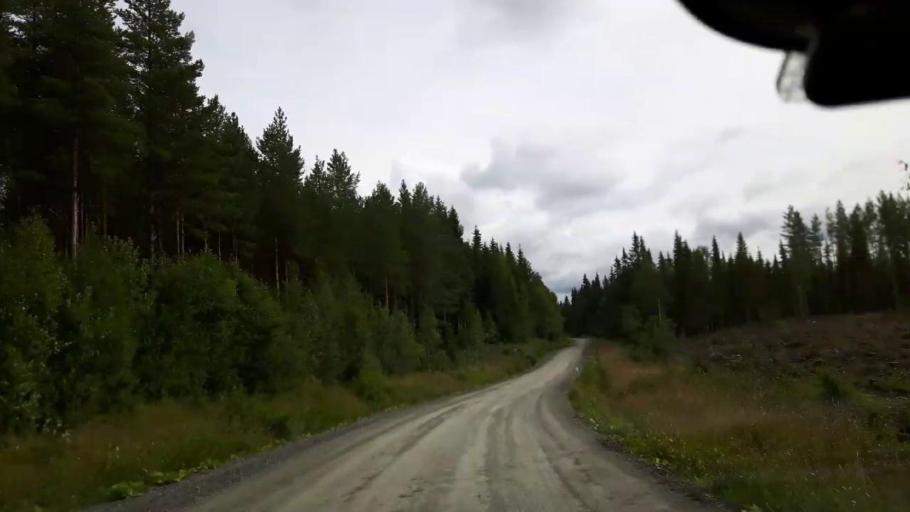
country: SE
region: Jaemtland
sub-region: Krokoms Kommun
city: Valla
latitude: 63.6401
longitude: 14.0028
